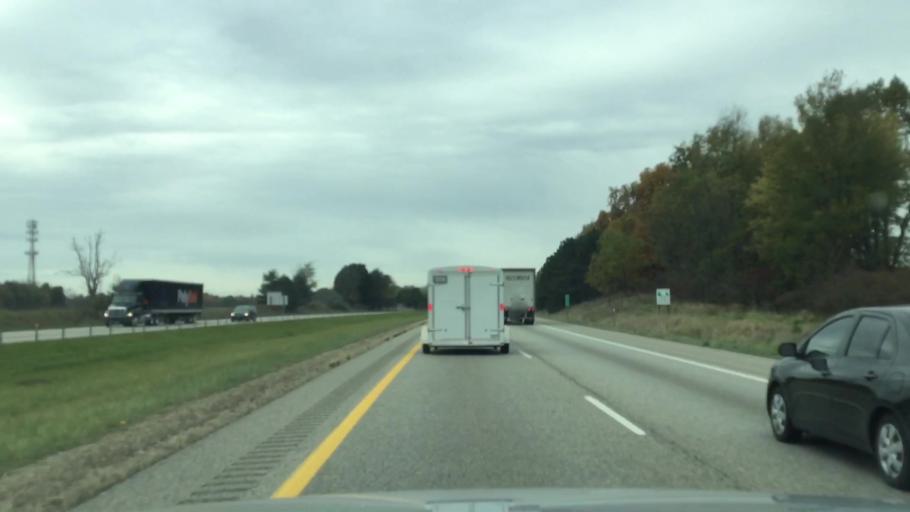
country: US
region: Michigan
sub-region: Calhoun County
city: Lakeview
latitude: 42.2657
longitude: -85.2583
